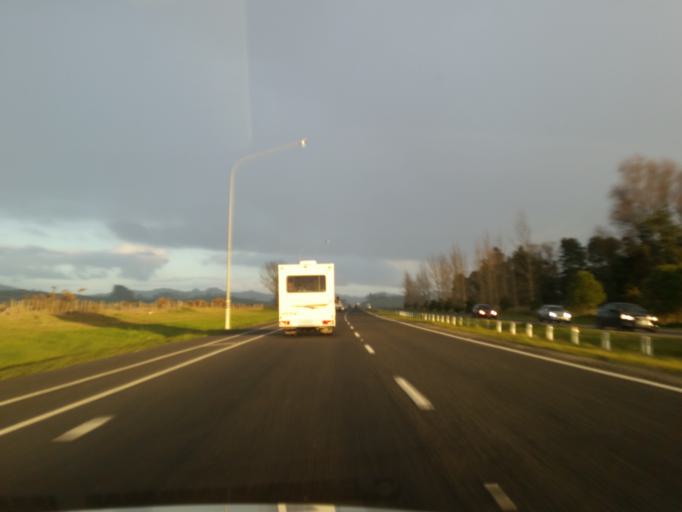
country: NZ
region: Waikato
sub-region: Waikato District
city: Te Kauwhata
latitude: -37.4943
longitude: 175.1624
